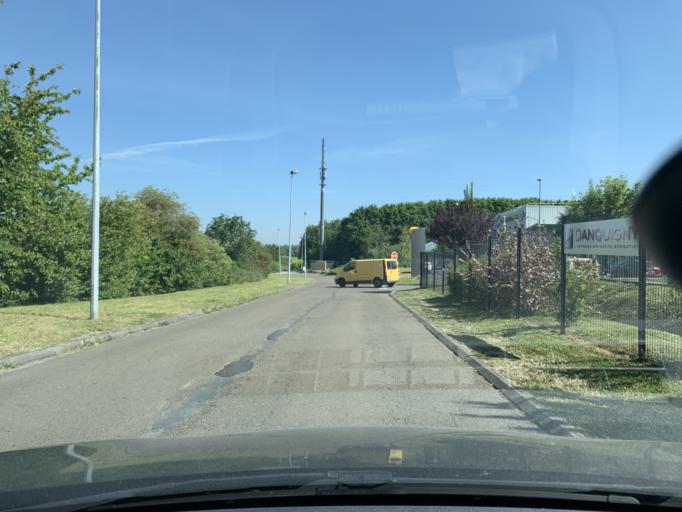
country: FR
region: Nord-Pas-de-Calais
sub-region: Departement du Nord
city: Cambrai
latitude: 50.1475
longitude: 3.2245
